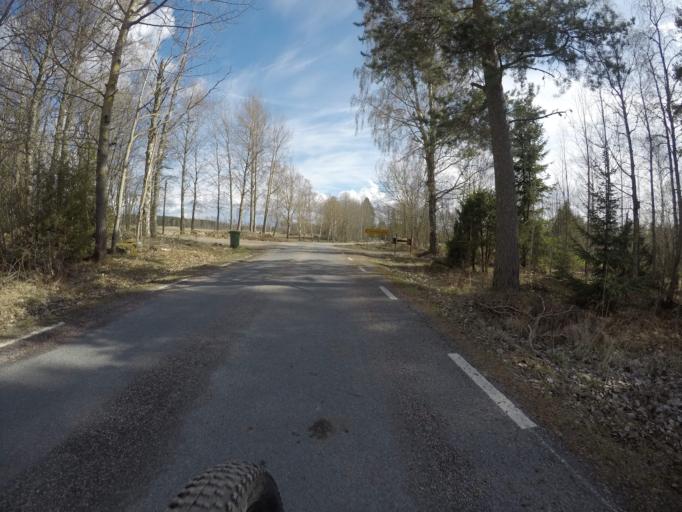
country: SE
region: Vaestmanland
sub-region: Kungsors Kommun
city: Kungsoer
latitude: 59.3092
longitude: 16.1236
